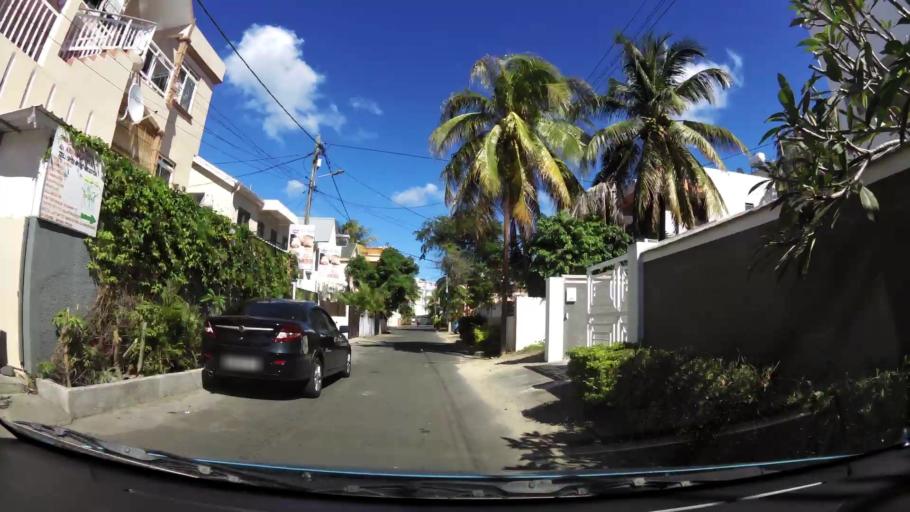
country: MU
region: Black River
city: Flic en Flac
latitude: -20.2771
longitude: 57.3700
